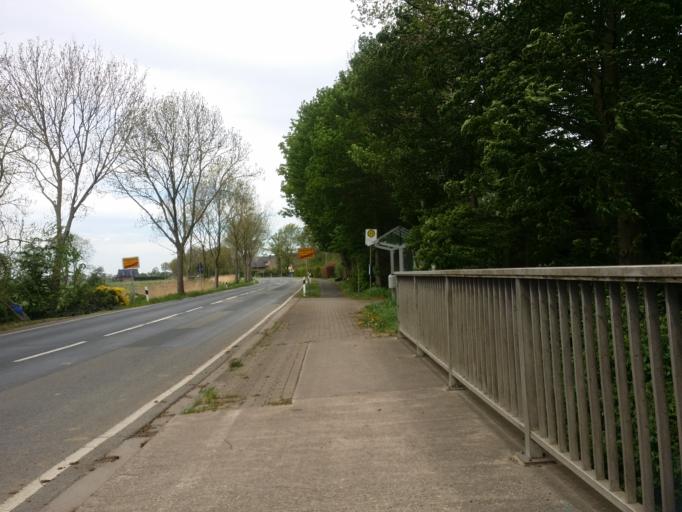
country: DE
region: Lower Saxony
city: Lemwerder
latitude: 53.1423
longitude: 8.5680
